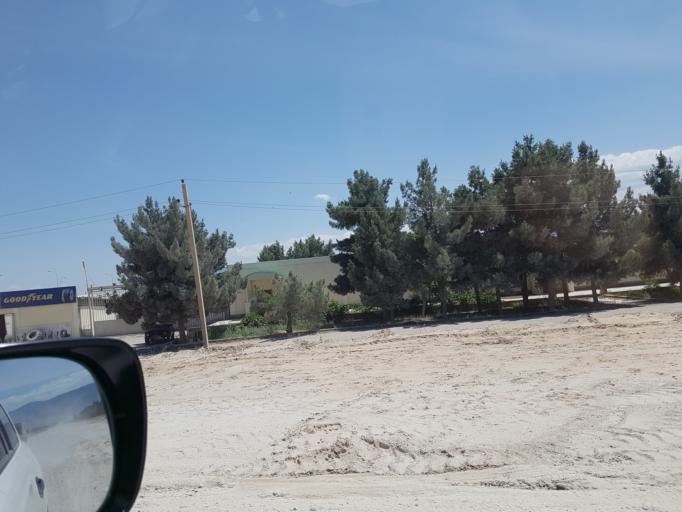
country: TM
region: Ahal
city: Abadan
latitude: 38.1750
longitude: 57.9564
